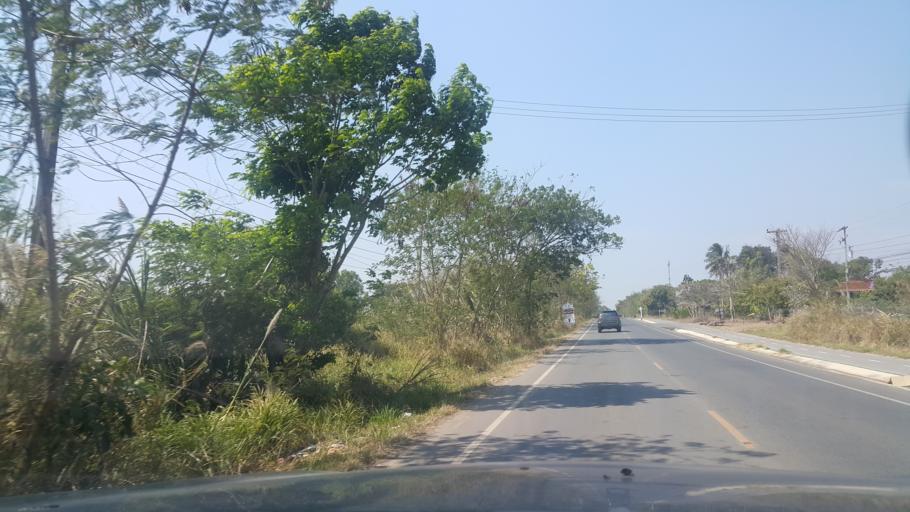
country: TH
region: Nakhon Ratchasima
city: Wang Nam Khiao
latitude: 14.3649
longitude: 101.9098
